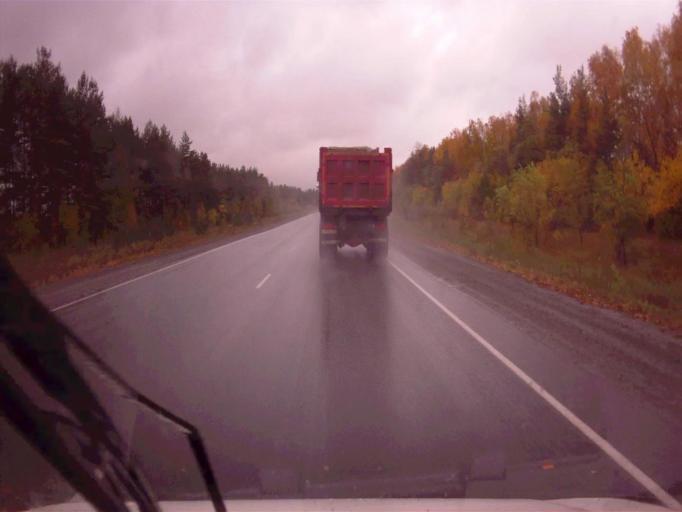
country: RU
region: Chelyabinsk
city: Roshchino
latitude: 55.3570
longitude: 61.2443
